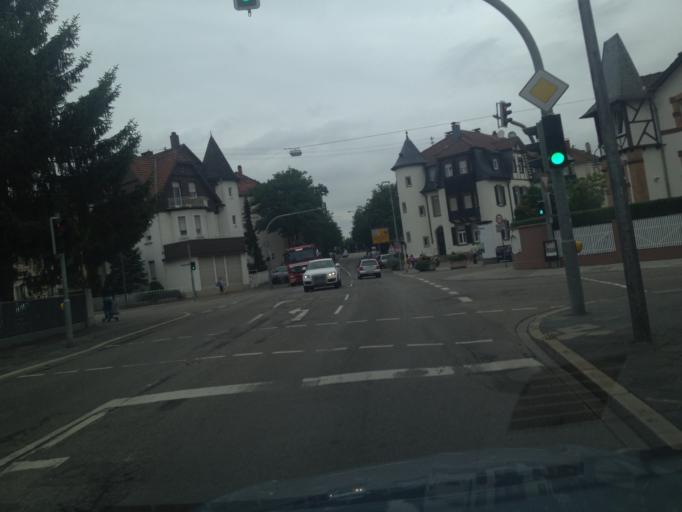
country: DE
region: Baden-Wuerttemberg
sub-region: Karlsruhe Region
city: Schwetzingen
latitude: 49.3853
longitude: 8.5820
